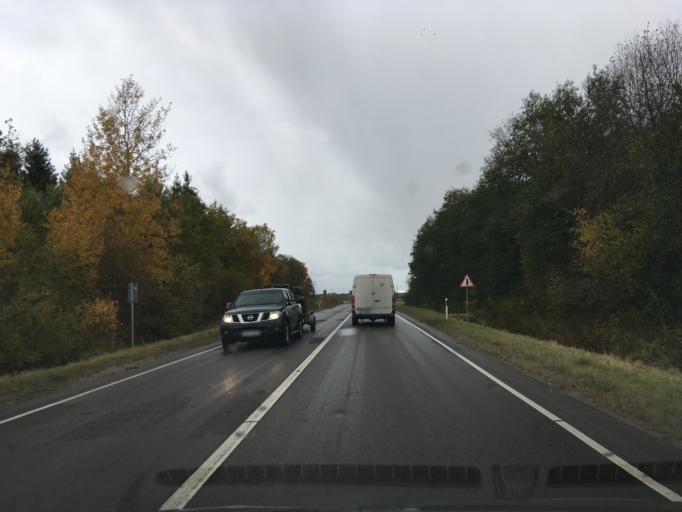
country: EE
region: Harju
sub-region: Anija vald
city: Kehra
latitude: 59.3440
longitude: 25.3122
